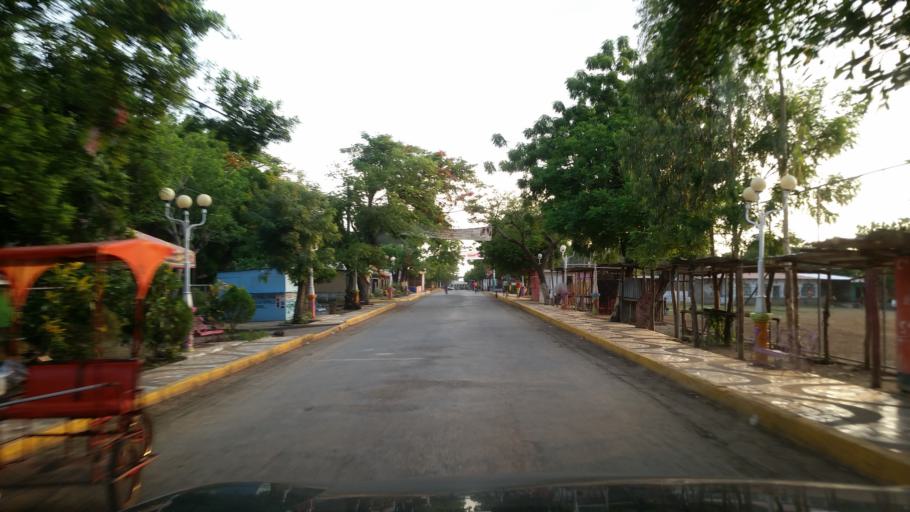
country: NI
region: Managua
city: Masachapa
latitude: 11.7850
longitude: -86.5141
